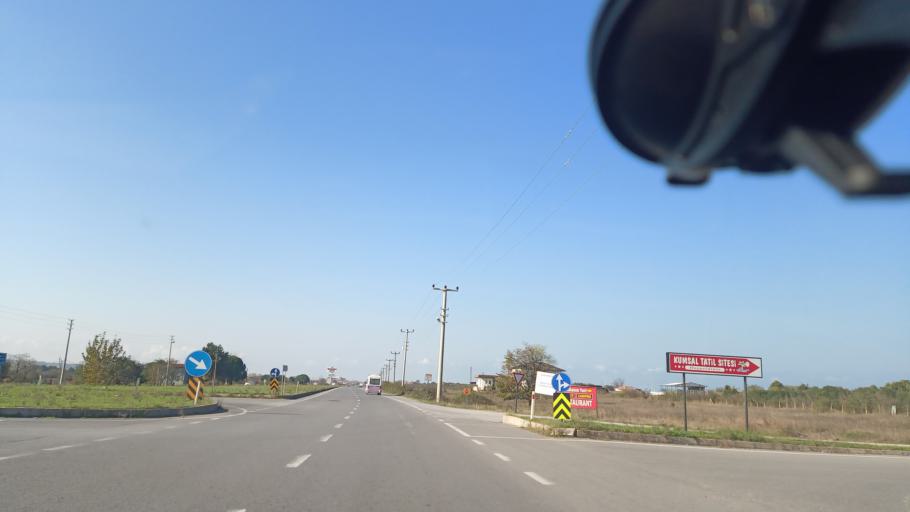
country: TR
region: Sakarya
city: Karasu
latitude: 41.0825
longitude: 30.7635
